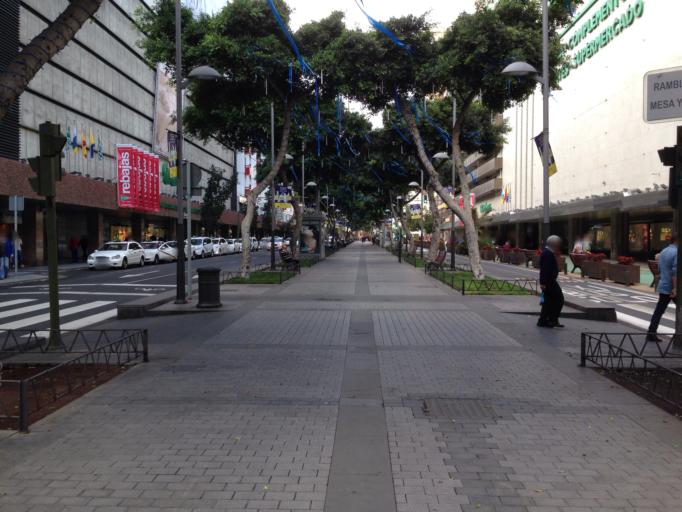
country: ES
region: Canary Islands
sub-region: Provincia de Las Palmas
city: Las Palmas de Gran Canaria
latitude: 28.1349
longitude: -15.4312
